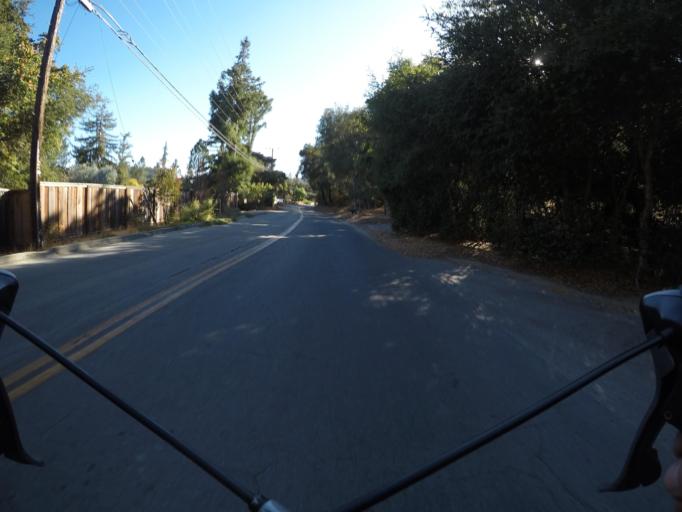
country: US
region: California
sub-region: Santa Cruz County
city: Ben Lomond
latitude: 37.0855
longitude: -122.0791
